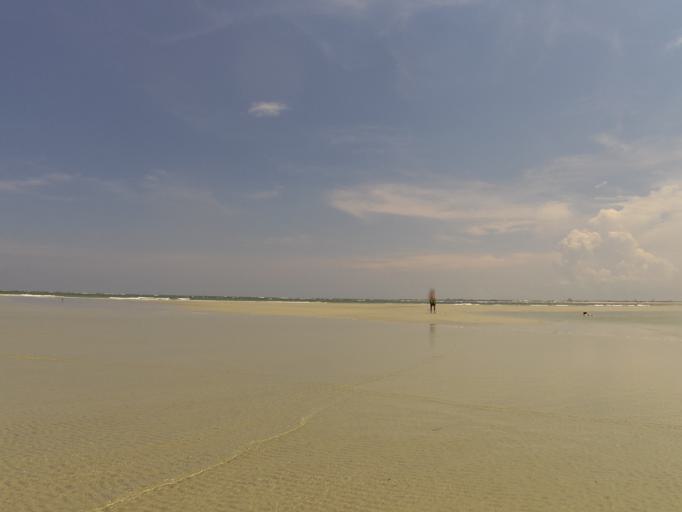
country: US
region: Florida
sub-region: Duval County
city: Atlantic Beach
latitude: 30.4352
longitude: -81.4052
